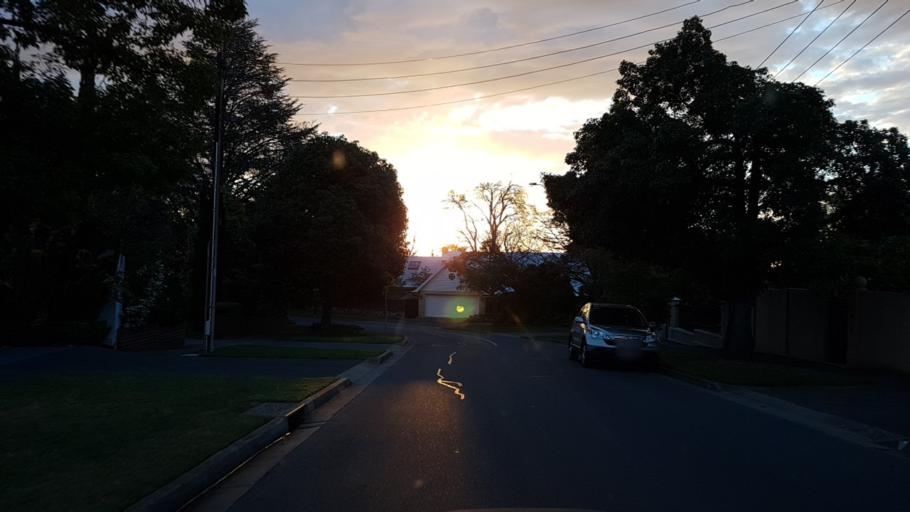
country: AU
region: South Australia
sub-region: Burnside
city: Linden Park
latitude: -34.9527
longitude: 138.6493
